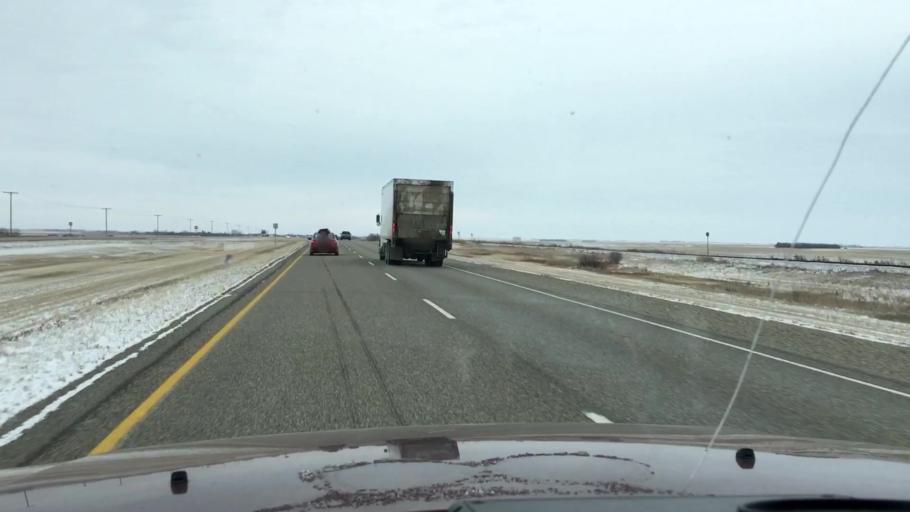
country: CA
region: Saskatchewan
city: Watrous
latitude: 51.1807
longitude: -105.9396
